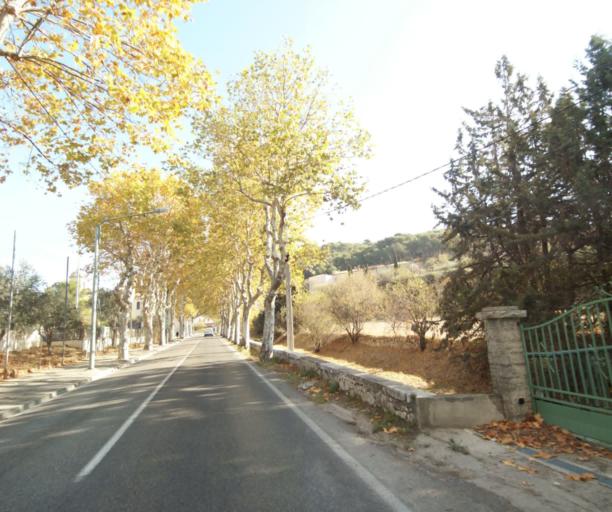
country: FR
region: Provence-Alpes-Cote d'Azur
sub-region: Departement des Bouches-du-Rhone
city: Allauch
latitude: 43.3572
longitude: 5.4889
